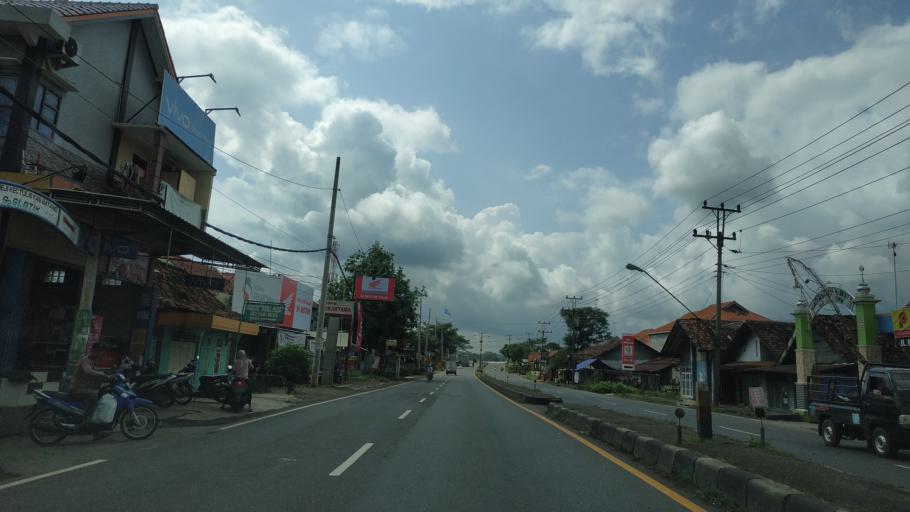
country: ID
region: Central Java
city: Pekalongan
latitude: -6.9521
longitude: 109.8038
